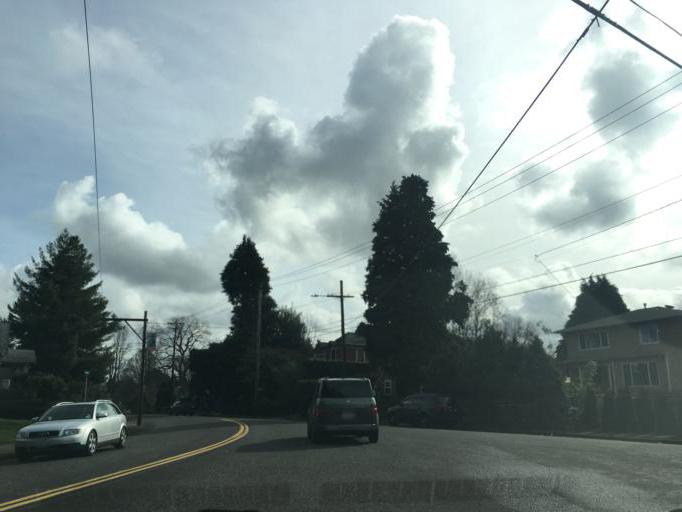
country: US
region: Oregon
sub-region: Clackamas County
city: Milwaukie
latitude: 45.4905
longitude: -122.6305
